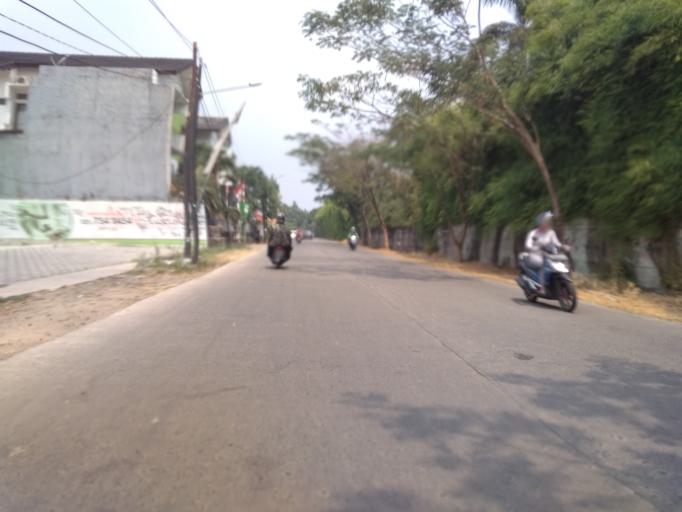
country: ID
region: West Java
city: Pamulang
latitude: -6.3169
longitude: 106.7893
